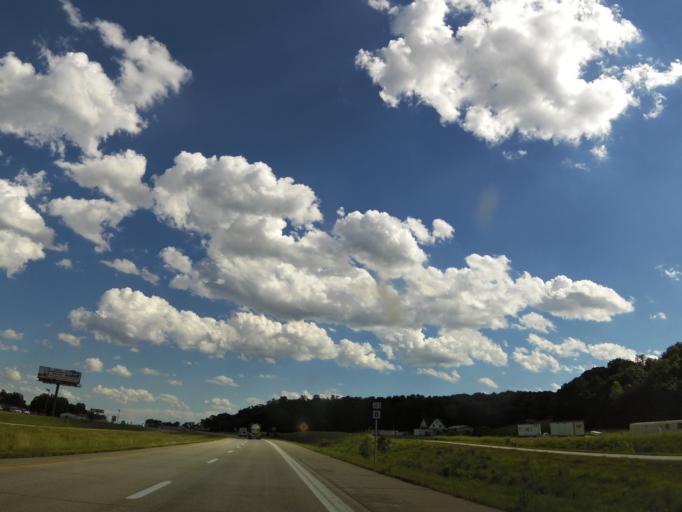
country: US
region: Missouri
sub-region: Clark County
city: Kahoka
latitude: 40.4575
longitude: -91.5694
